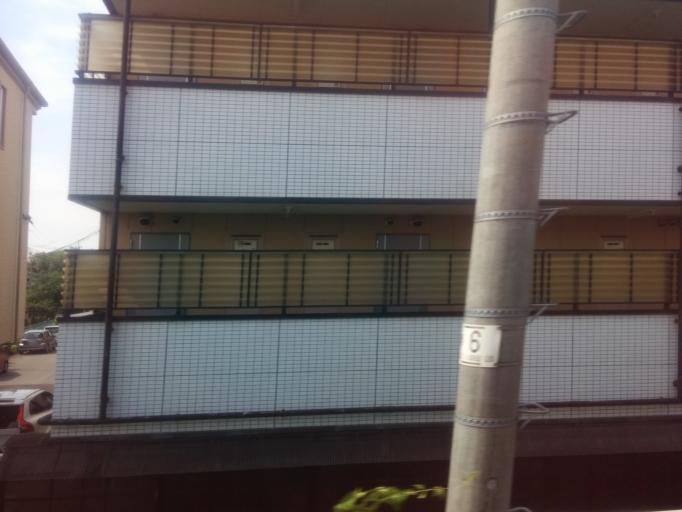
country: JP
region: Kyoto
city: Muko
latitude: 35.0185
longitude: 135.6838
